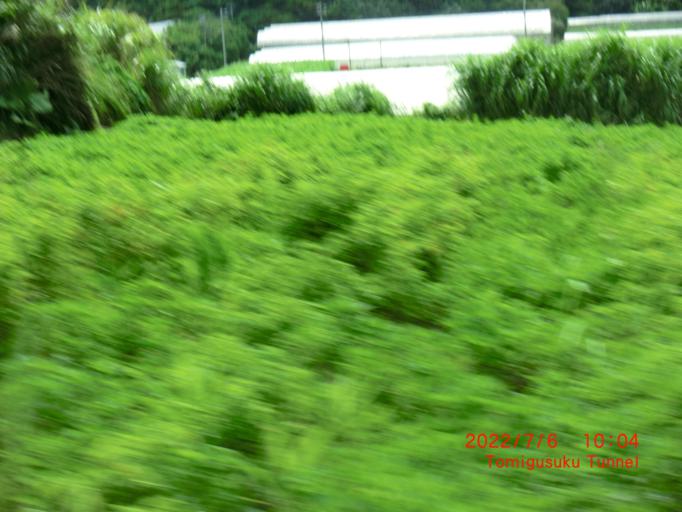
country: JP
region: Okinawa
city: Tomigusuku
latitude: 26.1683
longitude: 127.6848
